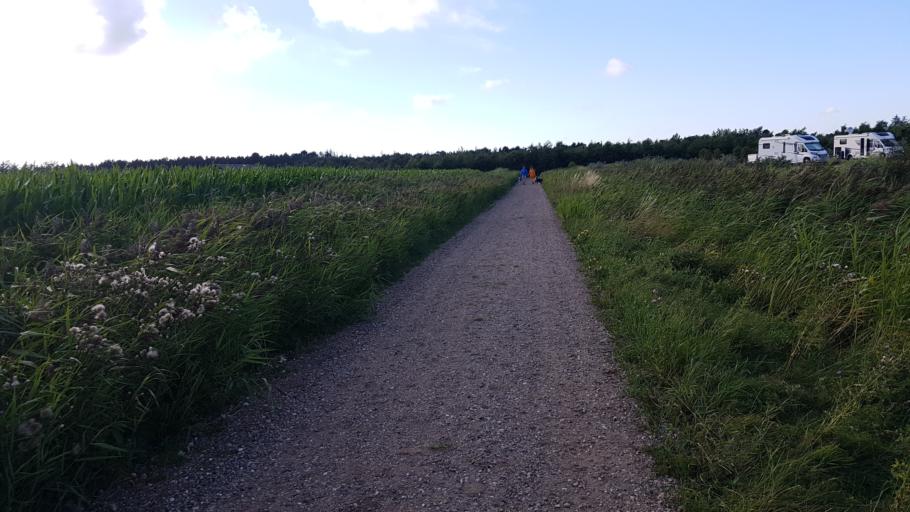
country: DE
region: Schleswig-Holstein
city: List
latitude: 55.0910
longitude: 8.5375
